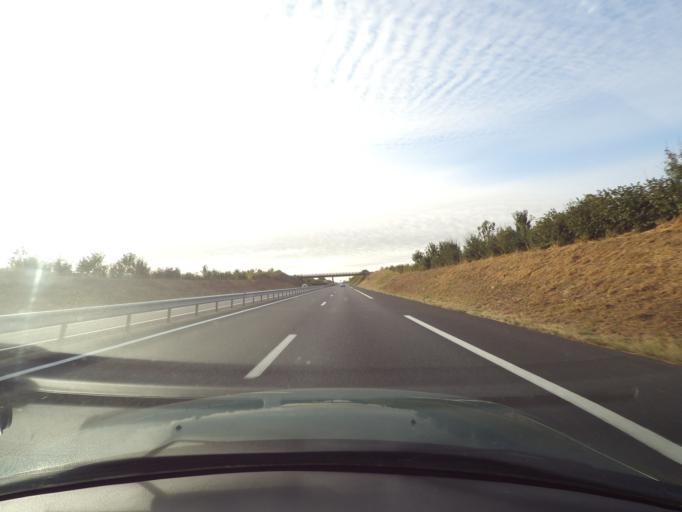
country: FR
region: Pays de la Loire
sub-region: Departement de Maine-et-Loire
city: La Tessoualle
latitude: 46.9952
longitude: -0.8559
